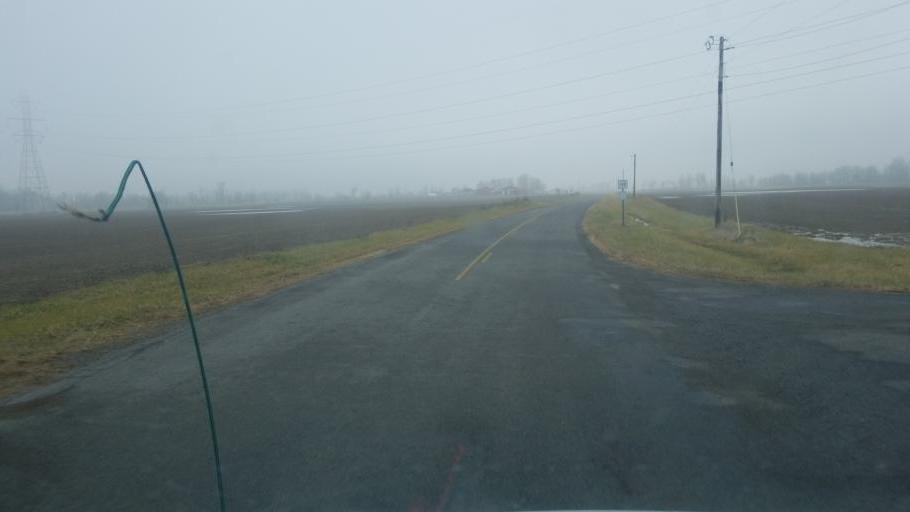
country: US
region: Ohio
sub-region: Hardin County
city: Kenton
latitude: 40.4721
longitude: -83.5451
